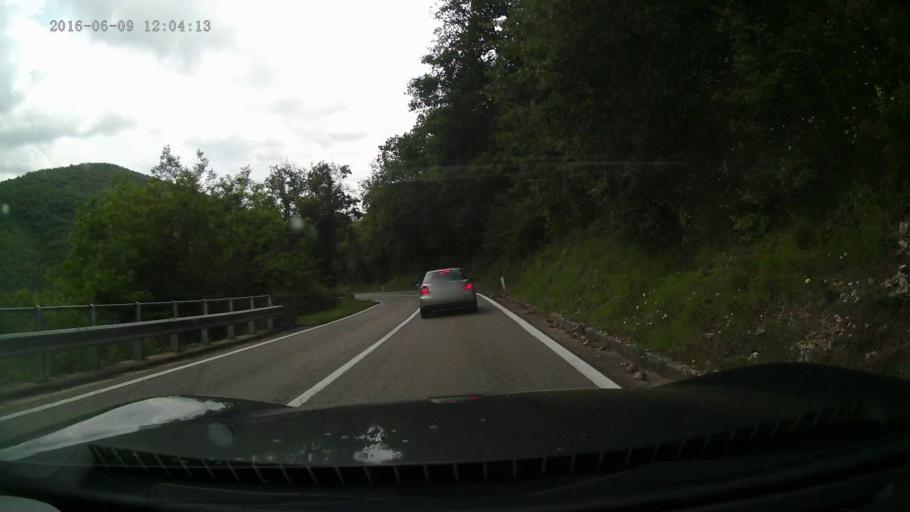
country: IT
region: Tuscany
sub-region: Province of Florence
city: Panzano in Chianti
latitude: 43.5223
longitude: 11.2984
